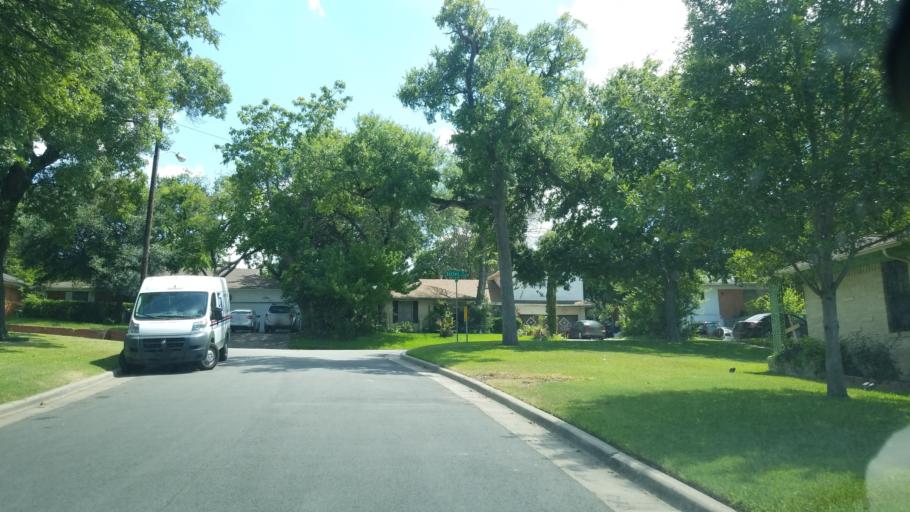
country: US
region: Texas
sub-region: Dallas County
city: Balch Springs
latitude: 32.7586
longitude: -96.6967
